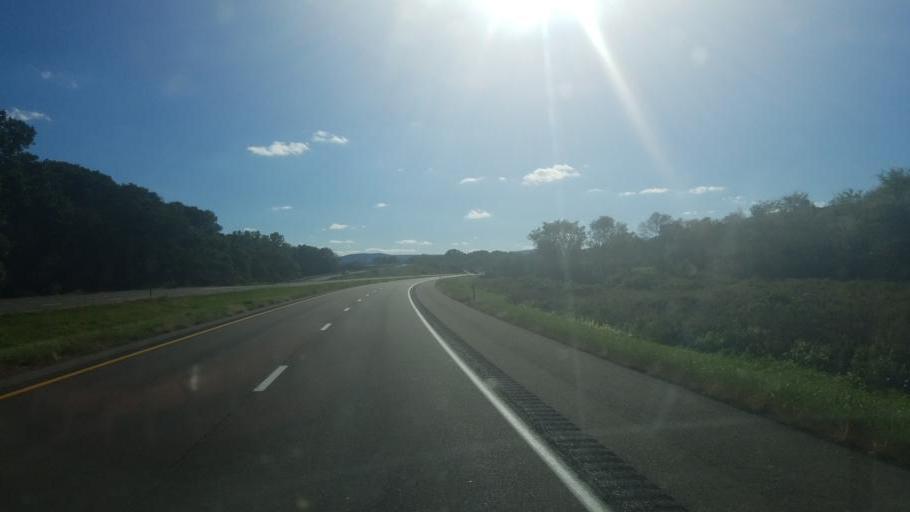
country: US
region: New York
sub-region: Cattaraugus County
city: Olean
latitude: 42.1039
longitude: -78.4214
